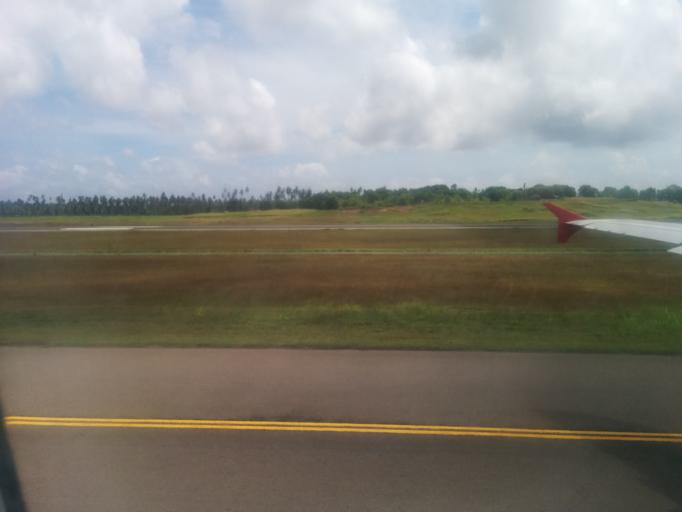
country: LK
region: Western
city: Katunayaka
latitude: 7.1884
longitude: 79.8915
